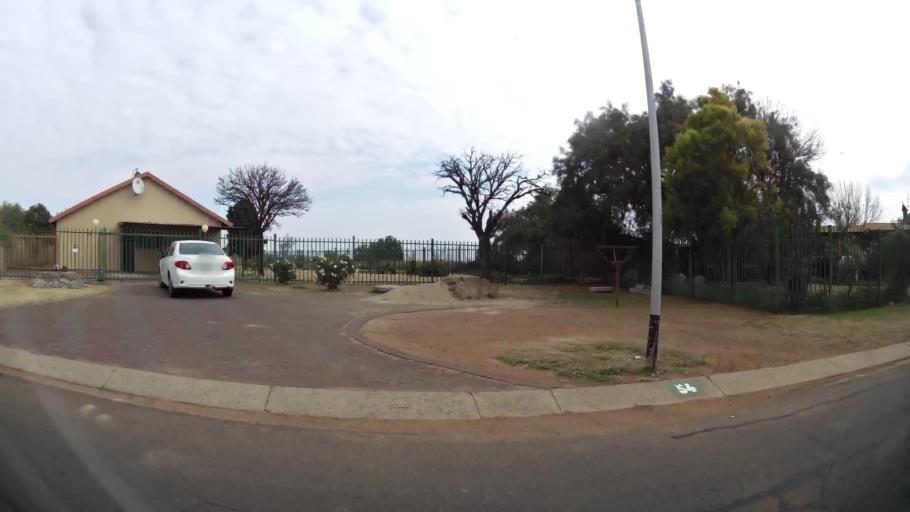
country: ZA
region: Orange Free State
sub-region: Mangaung Metropolitan Municipality
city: Bloemfontein
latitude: -29.1290
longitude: 26.1654
